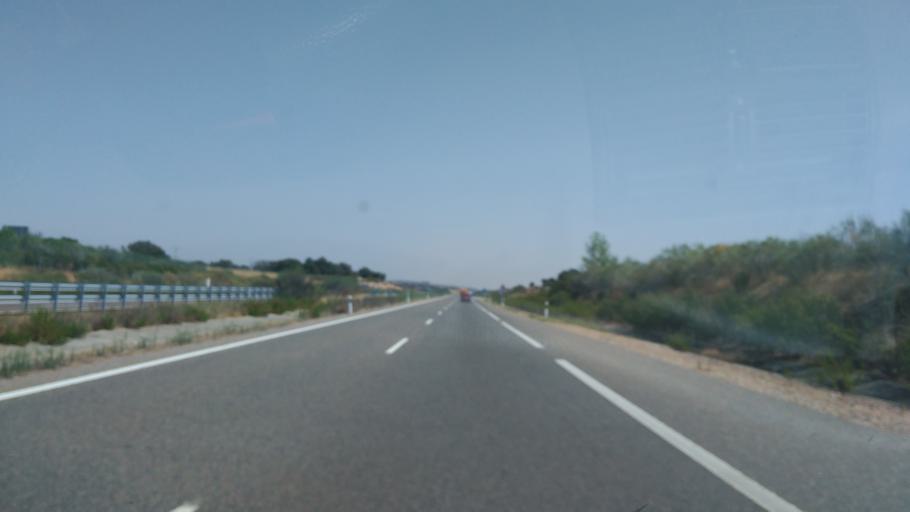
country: ES
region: Castille and Leon
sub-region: Provincia de Salamanca
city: San Munoz
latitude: 40.8205
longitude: -6.1184
